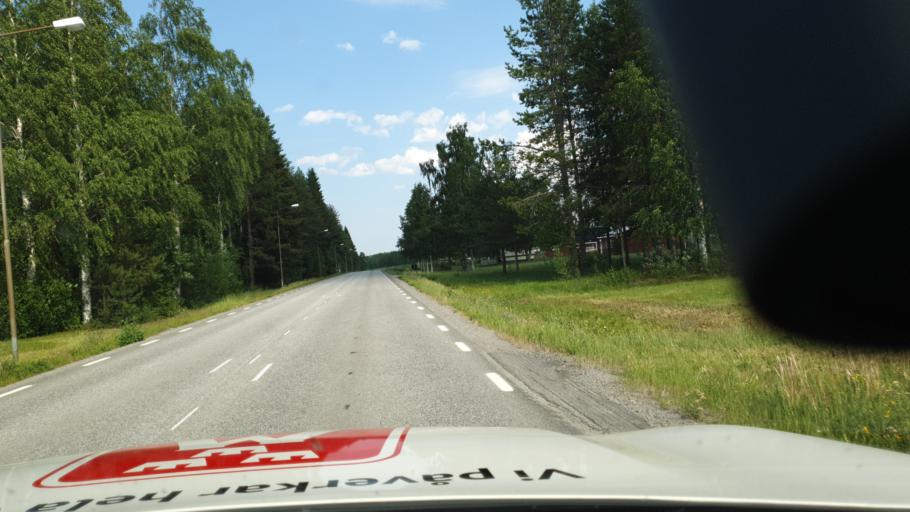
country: SE
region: Vaesterbotten
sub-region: Skelleftea Kommun
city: Viken
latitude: 64.7414
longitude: 20.8077
